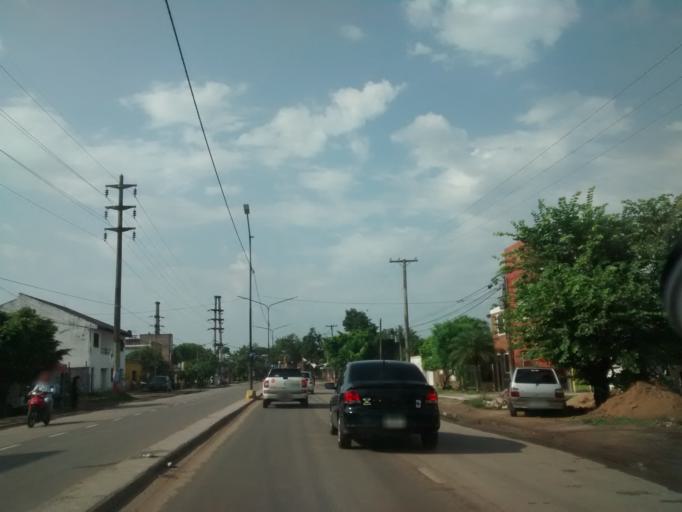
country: AR
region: Chaco
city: Resistencia
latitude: -27.4310
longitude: -58.9801
